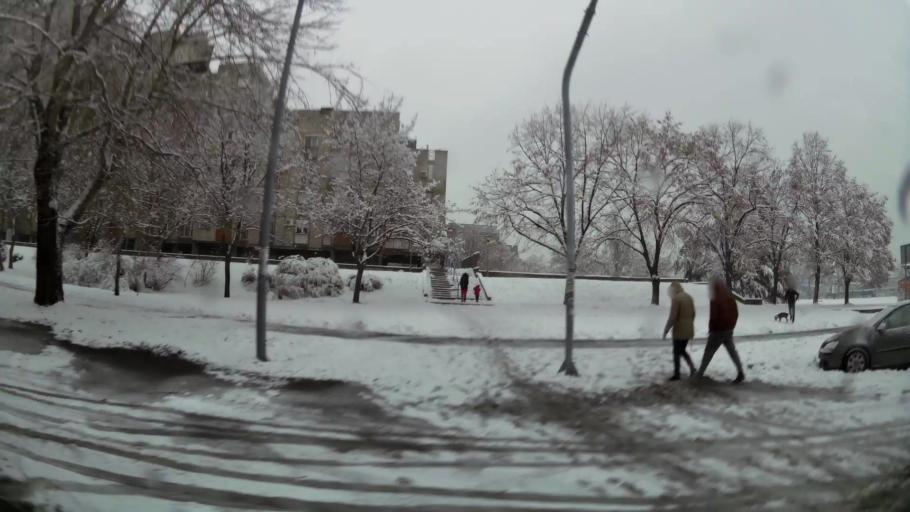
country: RS
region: Central Serbia
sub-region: Belgrade
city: Novi Beograd
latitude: 44.8029
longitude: 20.3802
